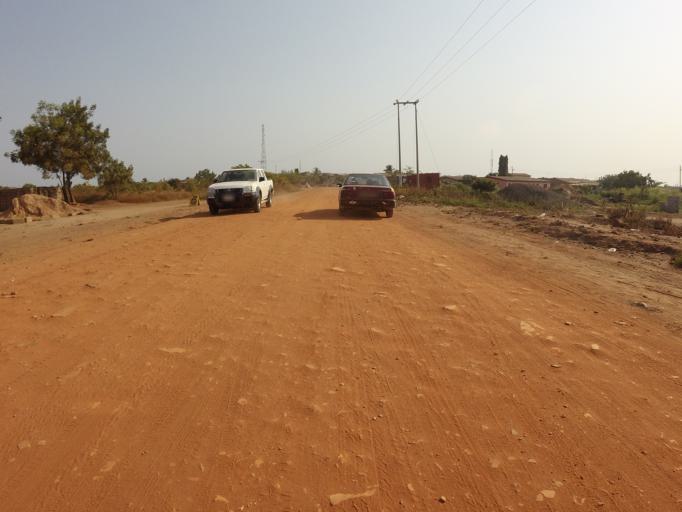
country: GH
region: Greater Accra
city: Tema
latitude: 5.7018
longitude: 0.0576
